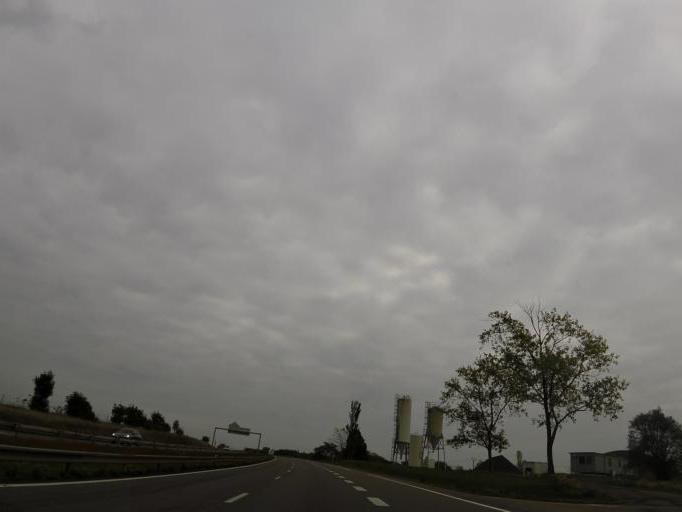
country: FR
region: Lorraine
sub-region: Departement de la Moselle
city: Retonfey
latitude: 49.1267
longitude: 6.2722
